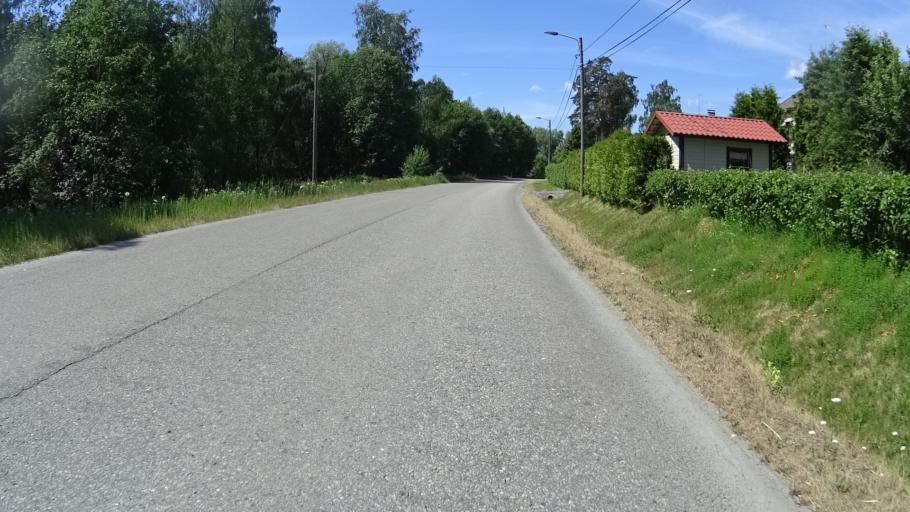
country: FI
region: Uusimaa
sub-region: Raaseporin
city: Karis
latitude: 60.0948
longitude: 23.6021
